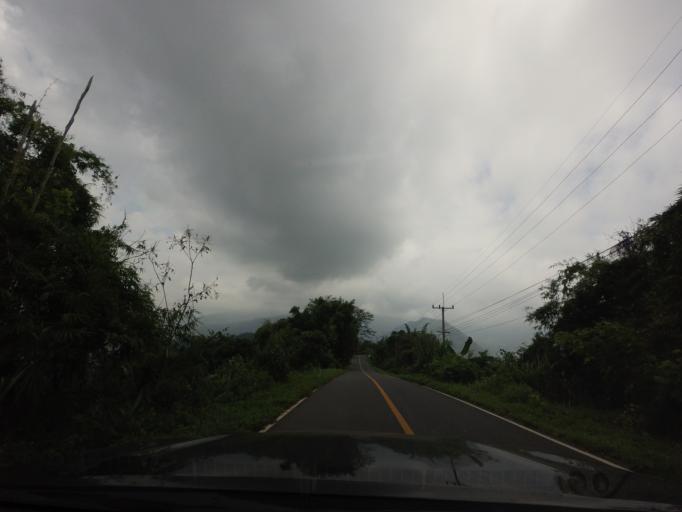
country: TH
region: Nan
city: Pua
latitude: 19.1879
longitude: 101.0349
